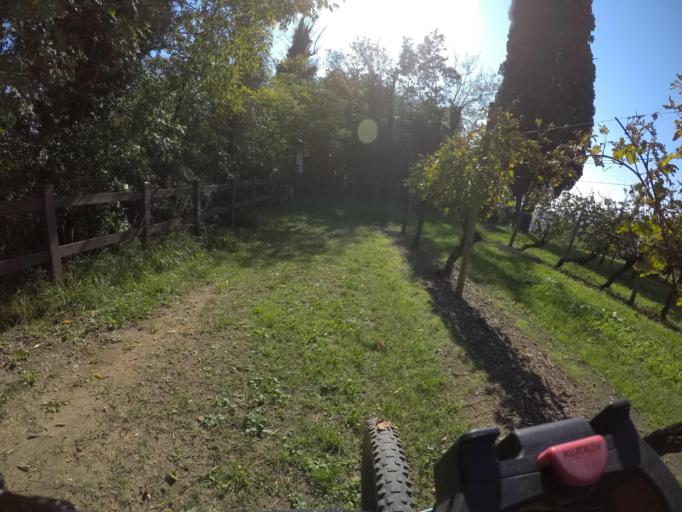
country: IT
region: Friuli Venezia Giulia
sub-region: Provincia di Udine
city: Manzano
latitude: 45.9944
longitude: 13.3852
